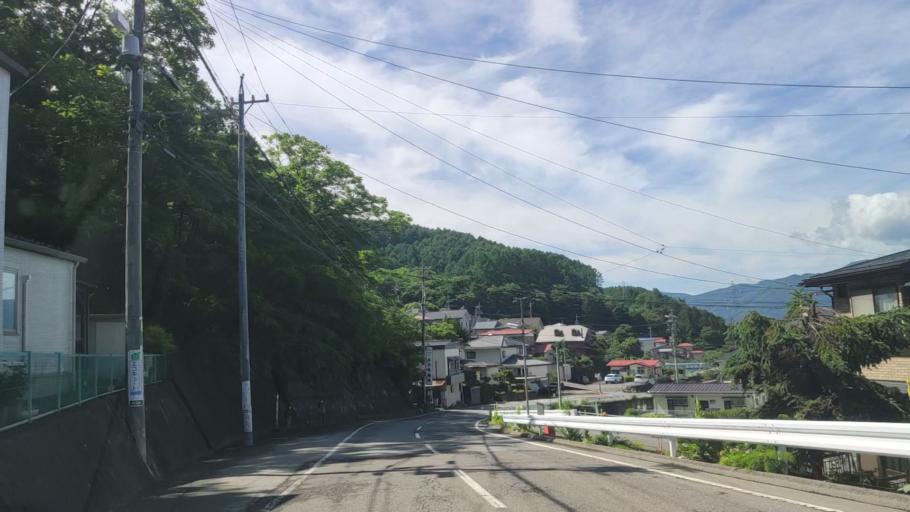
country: JP
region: Nagano
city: Suwa
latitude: 36.0479
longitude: 138.1281
